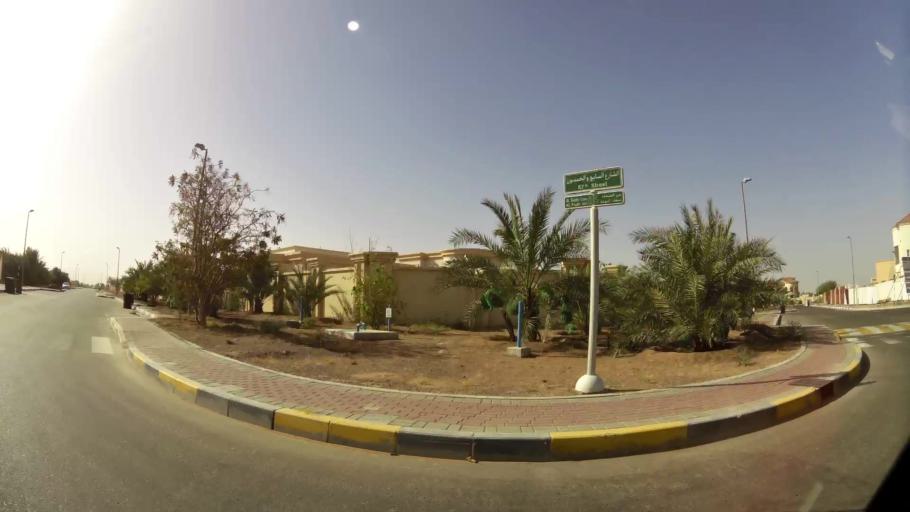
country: OM
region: Al Buraimi
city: Al Buraymi
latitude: 24.3487
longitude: 55.7985
